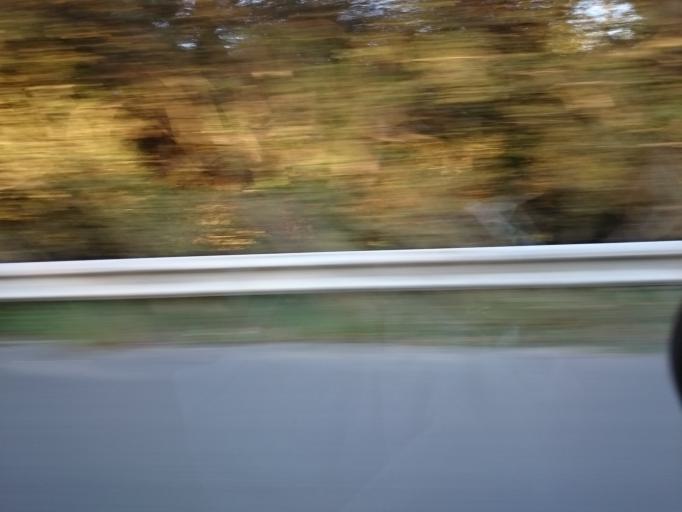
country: FR
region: Brittany
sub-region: Departement des Cotes-d'Armor
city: Plounevez-Moedec
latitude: 48.5632
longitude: -3.5230
